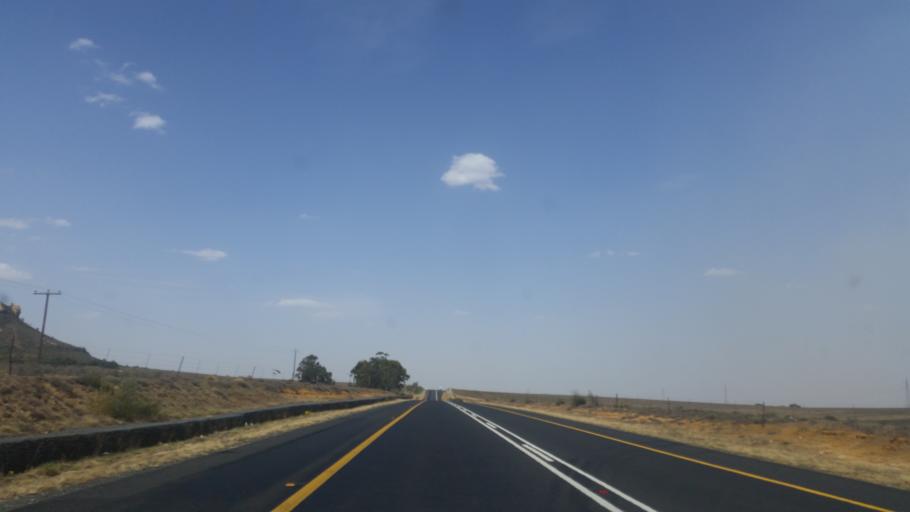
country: ZA
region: Orange Free State
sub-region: Thabo Mofutsanyana District Municipality
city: Bethlehem
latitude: -28.3021
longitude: 28.5562
